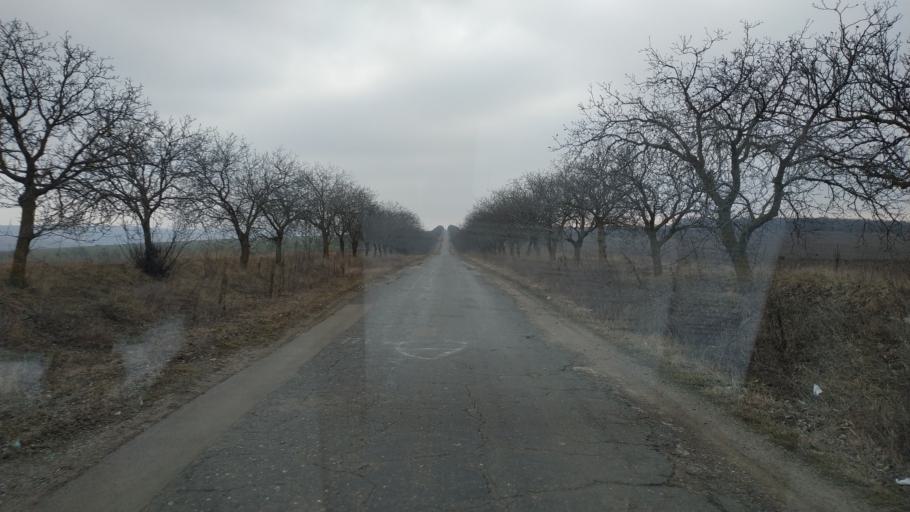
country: MD
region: Hincesti
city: Dancu
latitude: 46.9018
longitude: 28.3055
